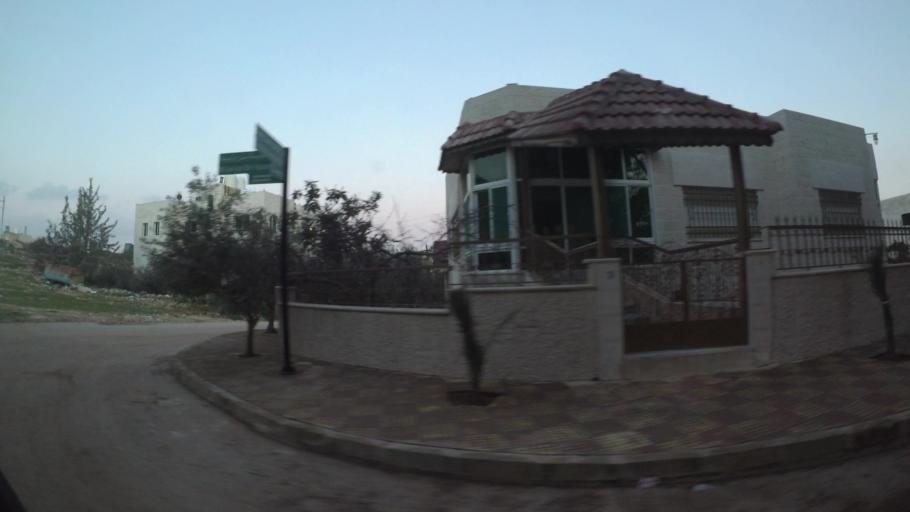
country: JO
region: Amman
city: Al Bunayyat ash Shamaliyah
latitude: 31.8896
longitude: 35.9209
